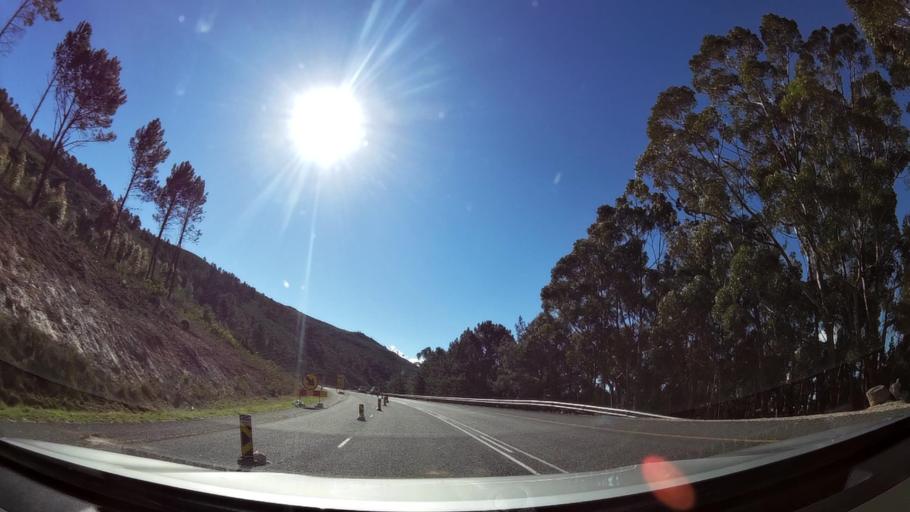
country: ZA
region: Western Cape
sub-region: Overberg District Municipality
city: Caledon
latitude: -34.2118
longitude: 19.5685
